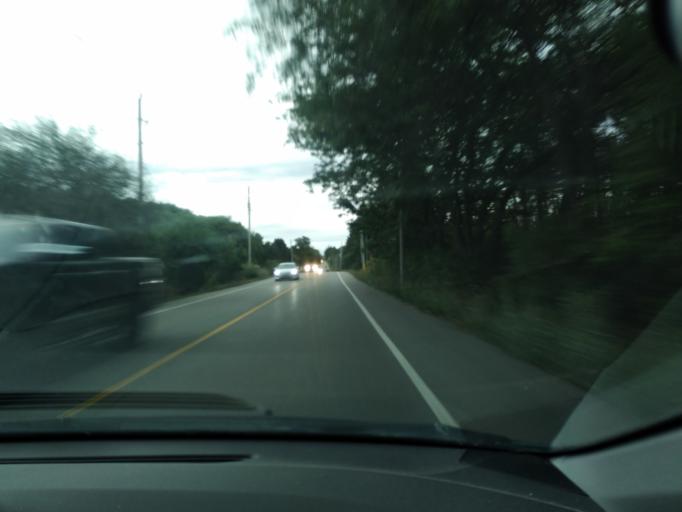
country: CA
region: Ontario
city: Bradford West Gwillimbury
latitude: 43.9736
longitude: -79.7960
